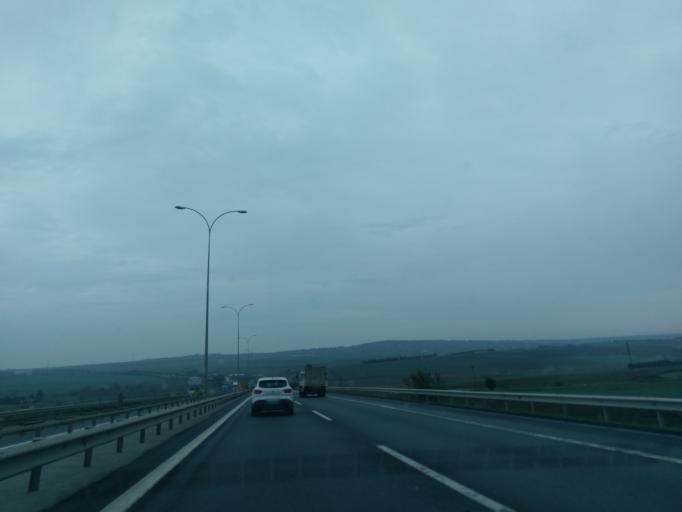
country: TR
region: Istanbul
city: Silivri
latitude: 41.1162
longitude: 28.2566
